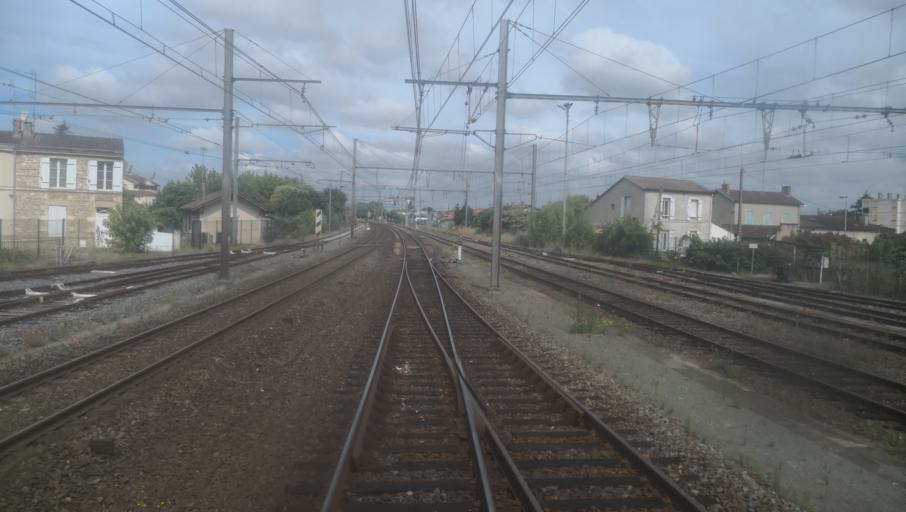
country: FR
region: Aquitaine
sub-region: Departement du Lot-et-Garonne
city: Marmande
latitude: 44.5057
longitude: 0.1639
